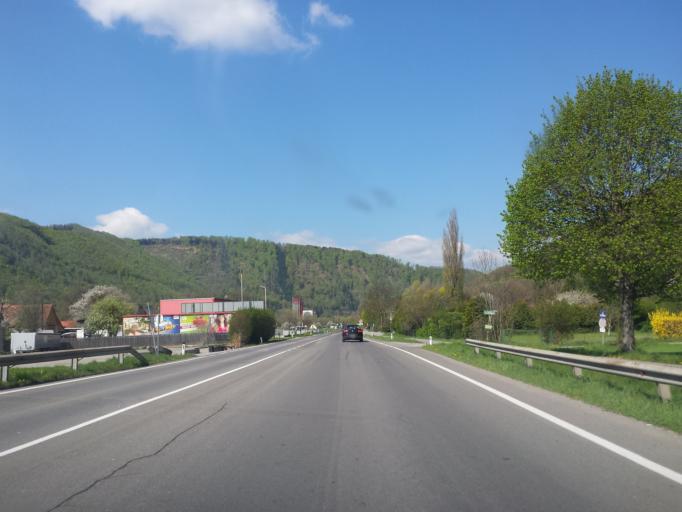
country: AT
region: Styria
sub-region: Graz Stadt
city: Goesting
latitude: 47.1098
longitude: 15.3941
